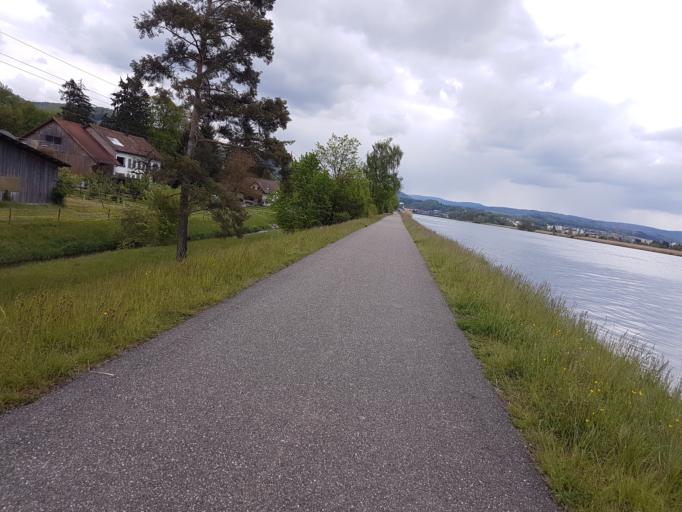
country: CH
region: Aargau
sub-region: Bezirk Zurzach
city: Klingnau
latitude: 47.5858
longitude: 8.2371
